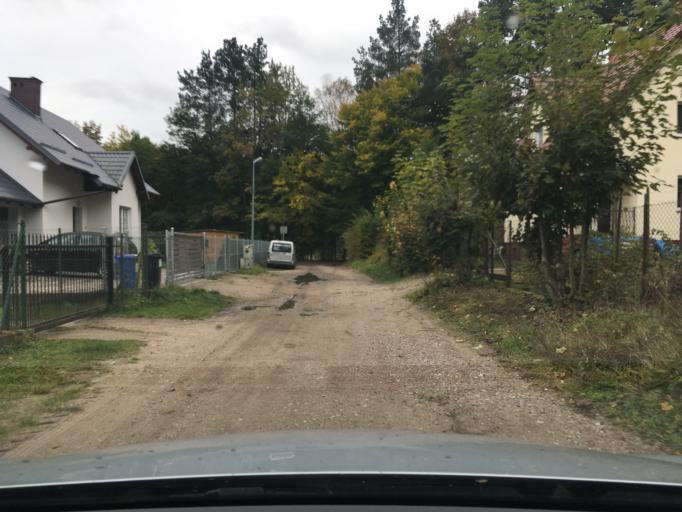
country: PL
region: Pomeranian Voivodeship
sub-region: Powiat koscierski
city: Koscierzyna
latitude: 54.0994
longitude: 17.9737
